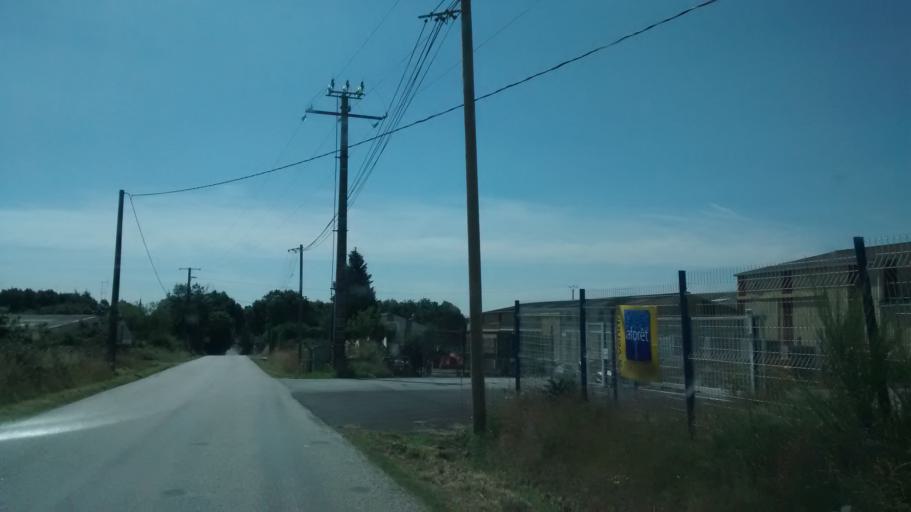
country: FR
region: Brittany
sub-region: Departement du Morbihan
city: Campeneac
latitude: 47.9632
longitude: -2.3023
